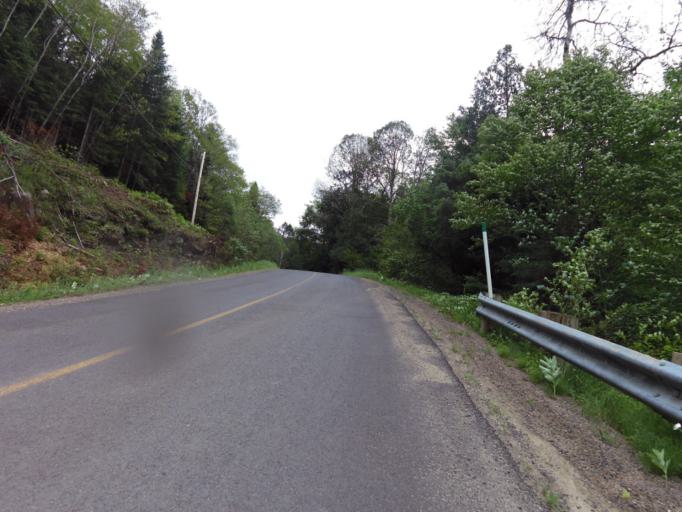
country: CA
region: Quebec
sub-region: Laurentides
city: Brownsburg-Chatham
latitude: 45.9114
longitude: -74.5975
